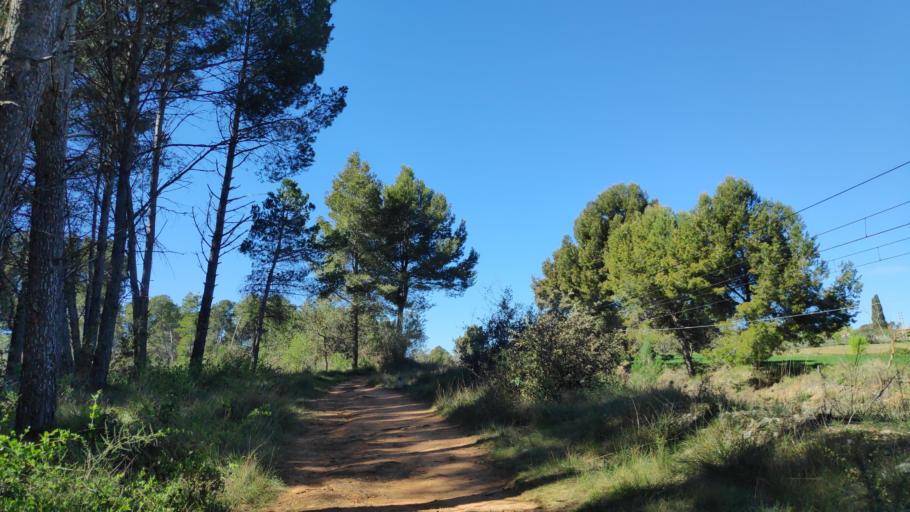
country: ES
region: Catalonia
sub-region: Provincia de Barcelona
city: Sant Quirze del Valles
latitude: 41.5646
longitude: 2.0683
